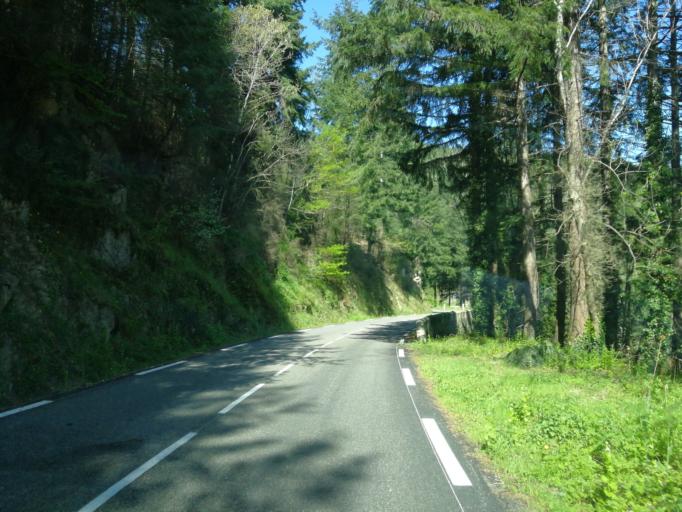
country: FR
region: Rhone-Alpes
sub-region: Departement de l'Ardeche
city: Le Cheylard
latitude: 44.8919
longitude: 4.4905
